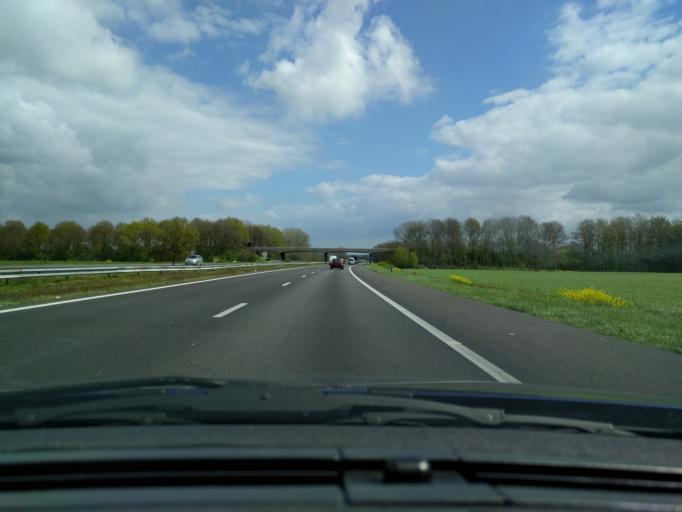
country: NL
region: North Brabant
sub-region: Gemeente Landerd
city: Schaijk
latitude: 51.7827
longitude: 5.6418
